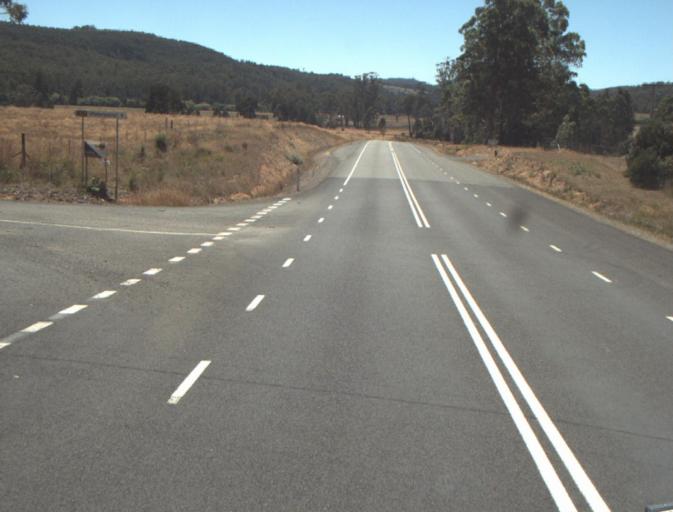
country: AU
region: Tasmania
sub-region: Launceston
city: Newstead
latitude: -41.3345
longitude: 147.3484
